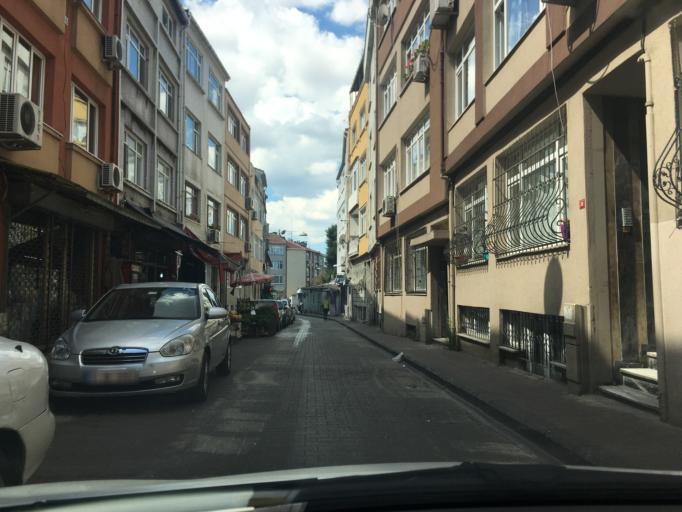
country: TR
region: Istanbul
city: Istanbul
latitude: 41.0142
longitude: 28.9273
